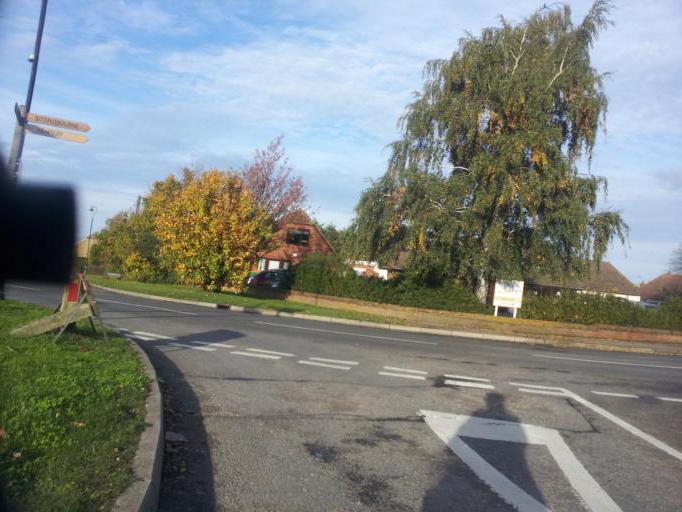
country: GB
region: England
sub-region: Kent
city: Sittingbourne
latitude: 51.3740
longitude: 0.7296
